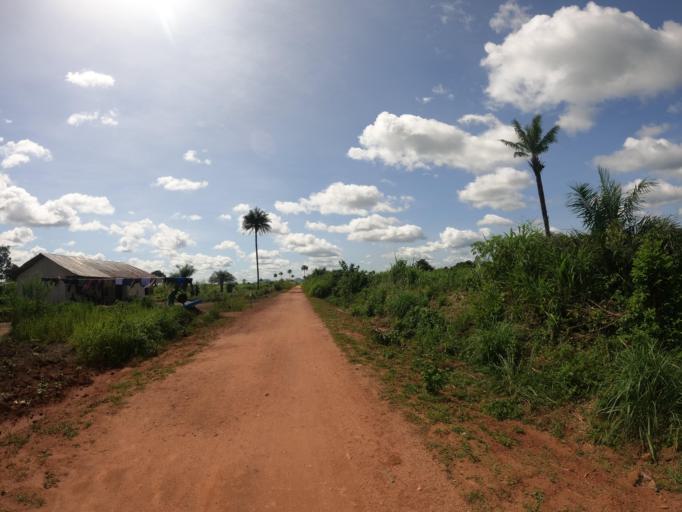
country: SL
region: Northern Province
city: Masingbi
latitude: 8.8333
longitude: -11.9951
